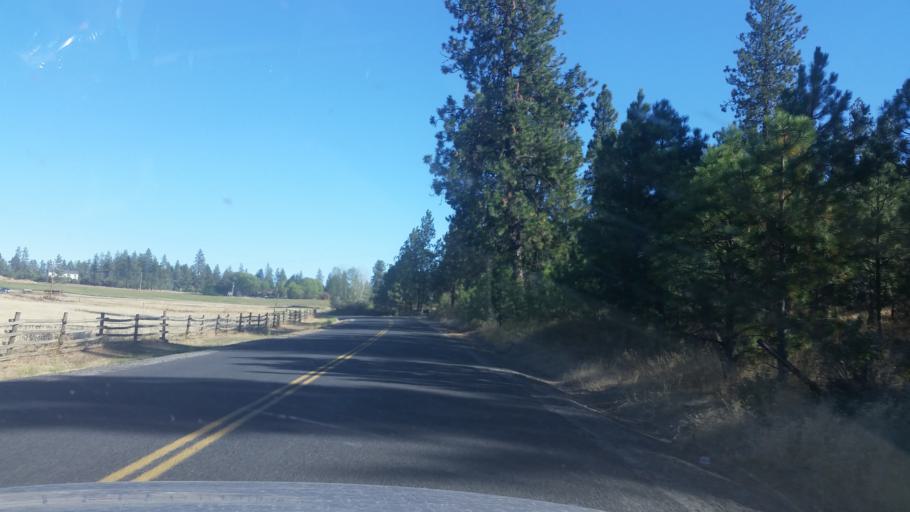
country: US
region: Washington
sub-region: Spokane County
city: Cheney
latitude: 47.5373
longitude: -117.4741
